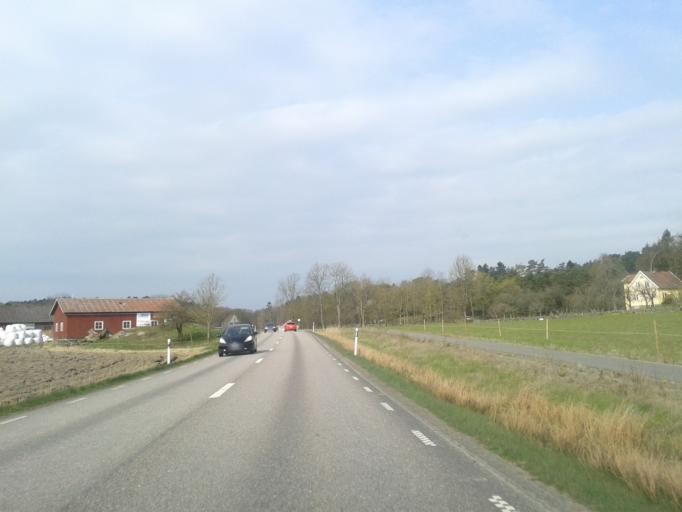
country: SE
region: Vaestra Goetaland
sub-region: Kungalvs Kommun
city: Kode
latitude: 57.8940
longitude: 11.8450
